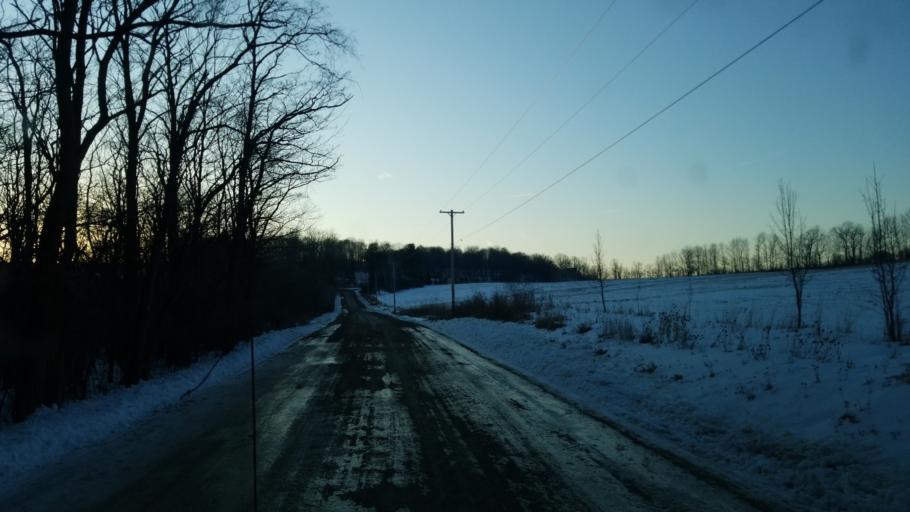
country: US
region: Pennsylvania
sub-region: Tioga County
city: Westfield
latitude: 42.0422
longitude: -77.6000
